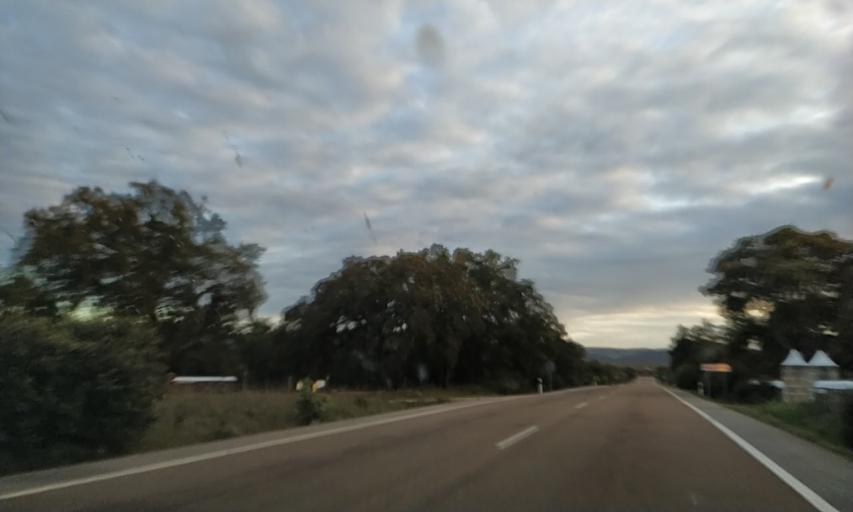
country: ES
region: Extremadura
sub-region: Provincia de Badajoz
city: Puebla de Obando
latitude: 39.2303
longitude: -6.5696
